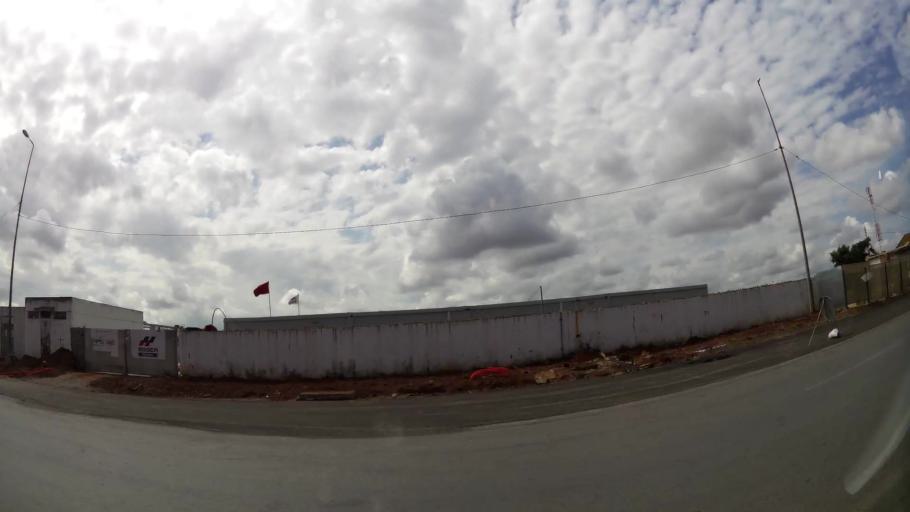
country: MA
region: Gharb-Chrarda-Beni Hssen
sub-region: Kenitra Province
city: Kenitra
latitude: 34.2518
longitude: -6.5843
